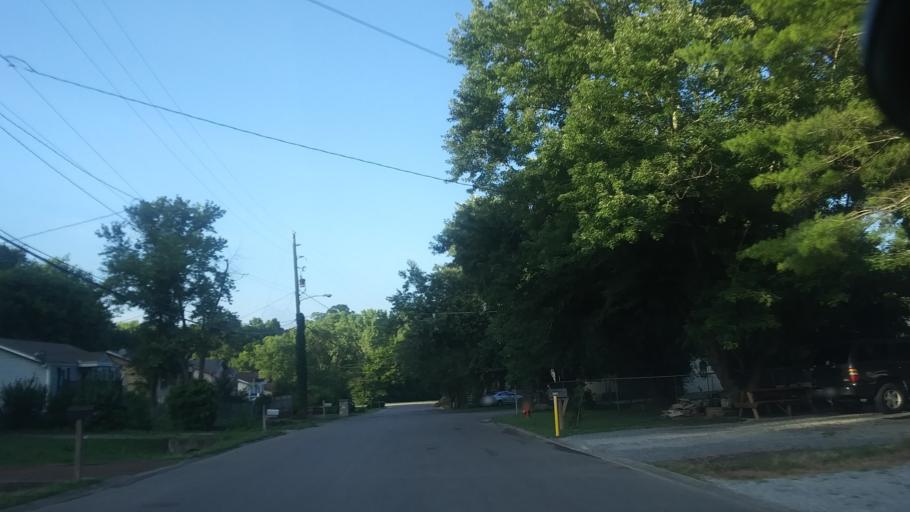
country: US
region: Tennessee
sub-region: Rutherford County
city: La Vergne
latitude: 36.0726
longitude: -86.6687
